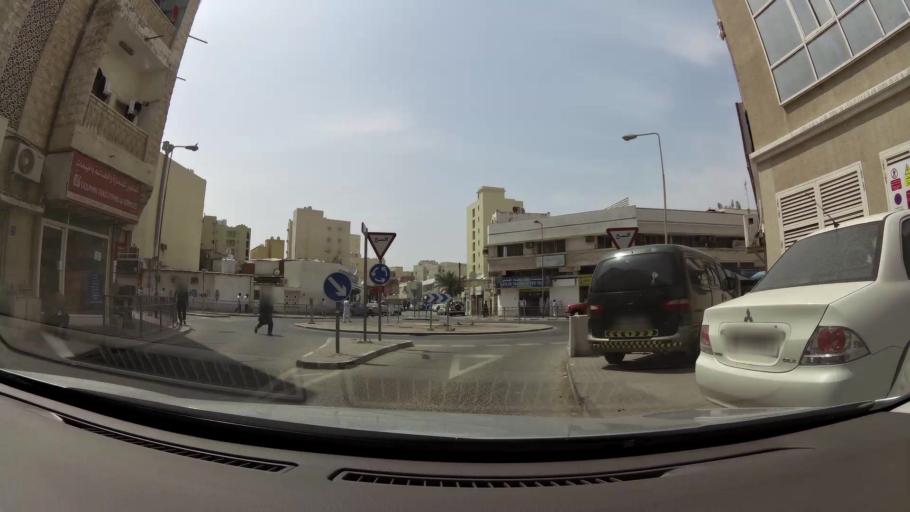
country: QA
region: Baladiyat ad Dawhah
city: Doha
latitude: 25.2805
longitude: 51.5402
